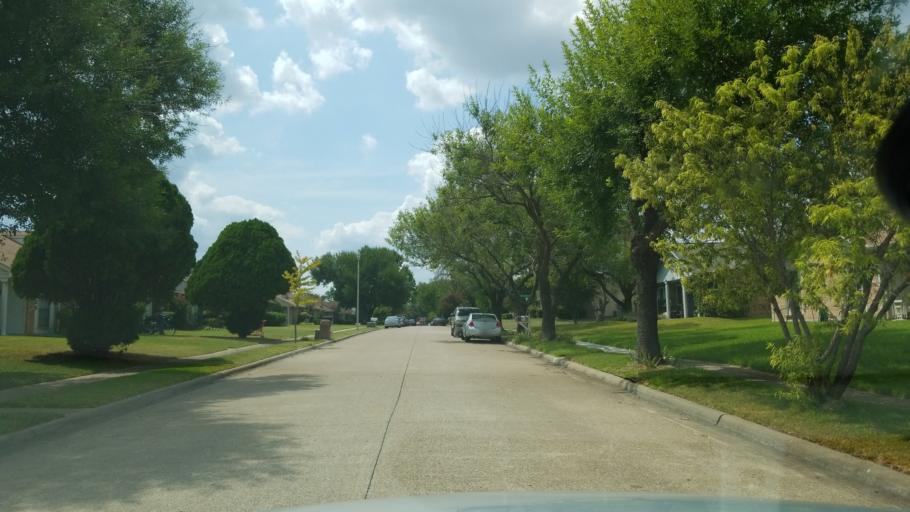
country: US
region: Texas
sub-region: Dallas County
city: Garland
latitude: 32.9217
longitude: -96.6684
